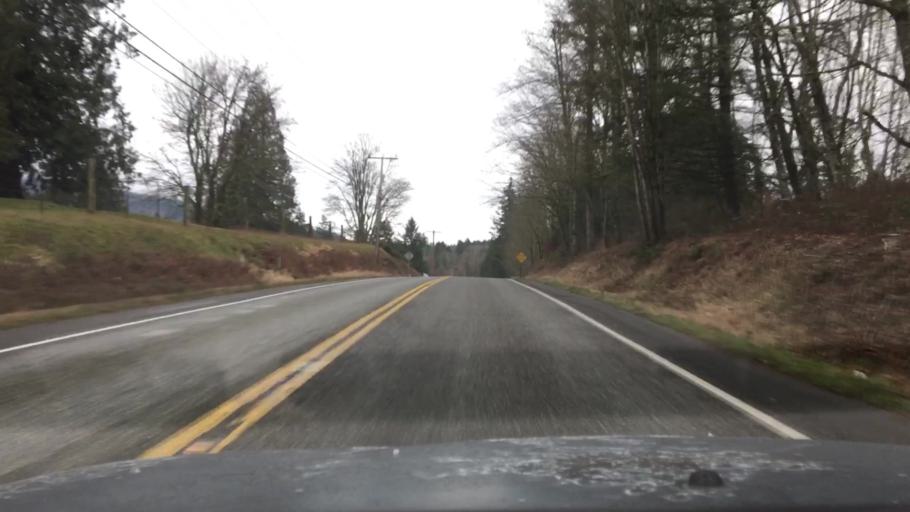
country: US
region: Washington
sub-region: Whatcom County
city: Sudden Valley
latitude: 48.6520
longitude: -122.3244
